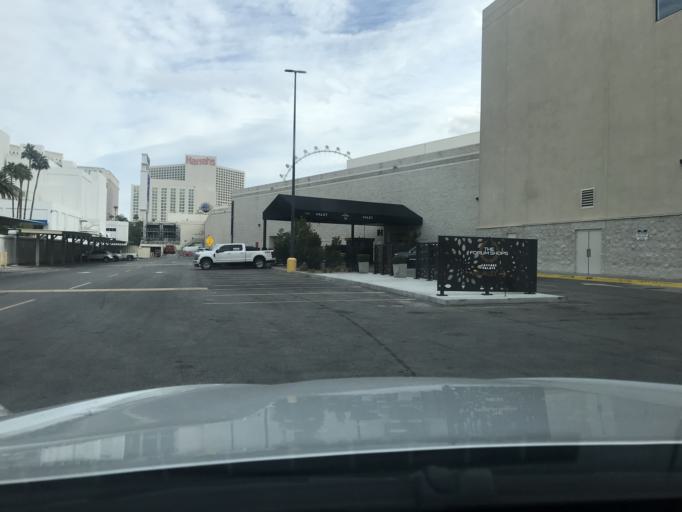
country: US
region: Nevada
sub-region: Clark County
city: Paradise
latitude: 36.1196
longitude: -115.1772
